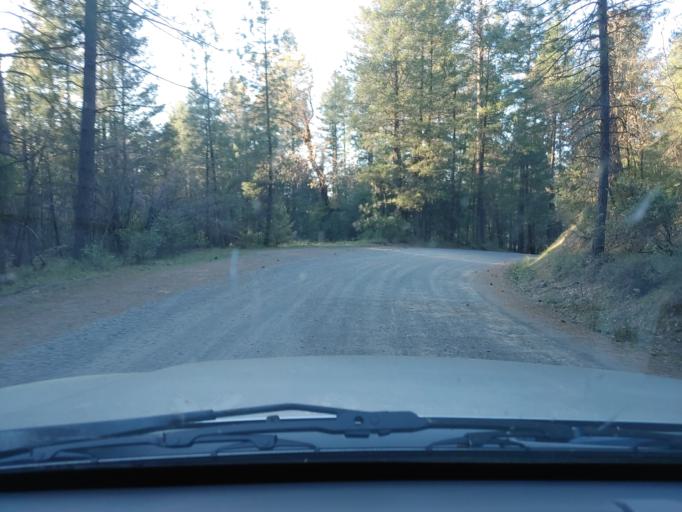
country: US
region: California
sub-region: Shasta County
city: Bella Vista
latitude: 40.8248
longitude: -122.0182
